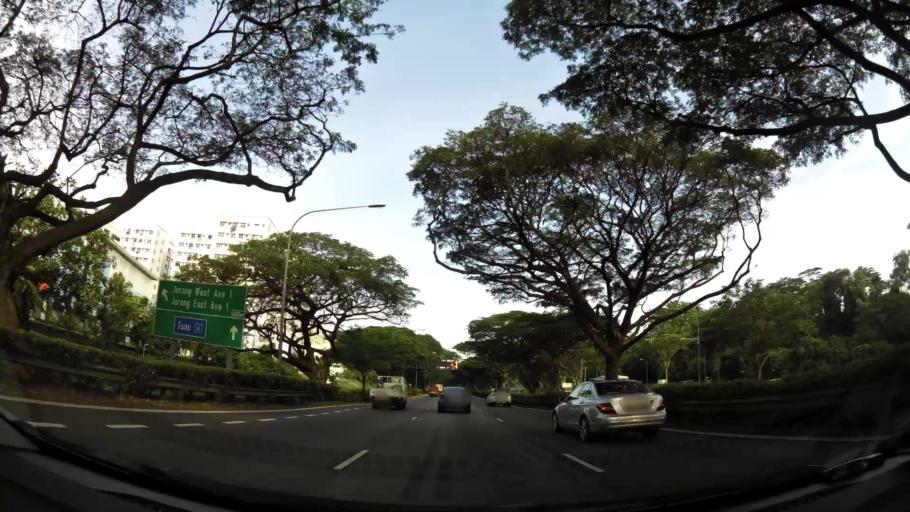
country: MY
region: Johor
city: Johor Bahru
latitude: 1.3494
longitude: 103.7336
